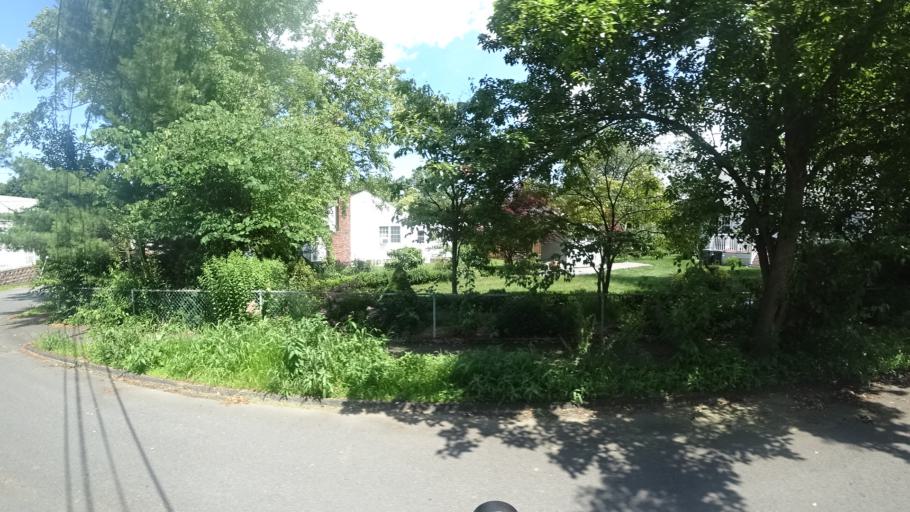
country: US
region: Massachusetts
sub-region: Norfolk County
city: Dedham
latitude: 42.2725
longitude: -71.1768
